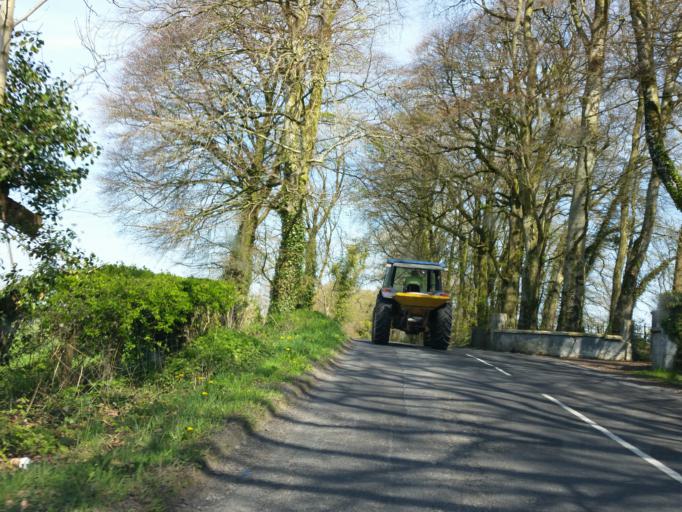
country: GB
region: Northern Ireland
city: Lisnaskea
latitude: 54.2862
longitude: -7.4254
